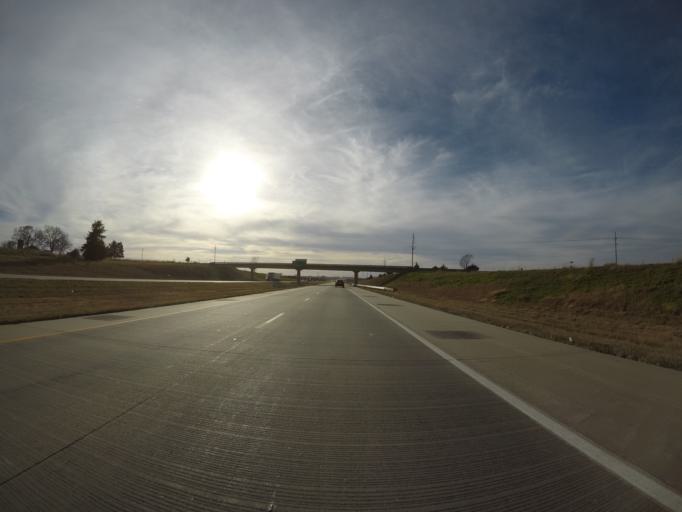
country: US
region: Kansas
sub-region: Franklin County
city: Ottawa
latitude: 38.5824
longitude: -95.2483
